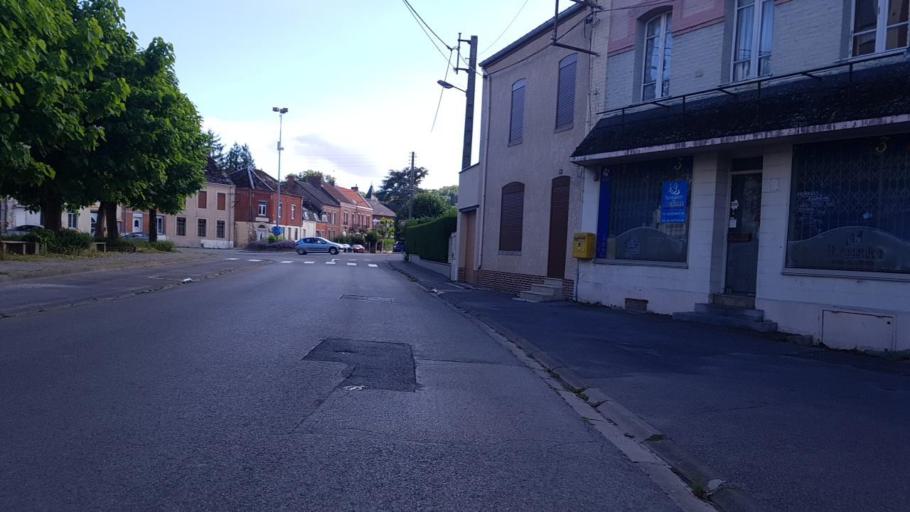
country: FR
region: Picardie
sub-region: Departement de l'Aisne
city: Hirson
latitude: 49.9215
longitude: 4.0781
